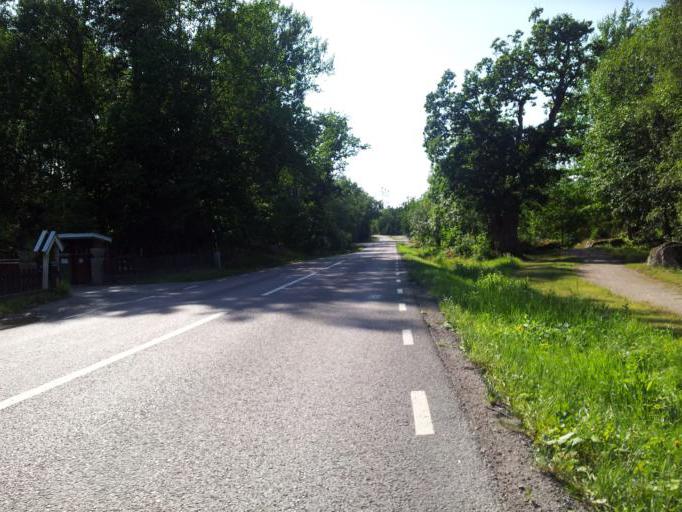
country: SE
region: Stockholm
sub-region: Norrtalje Kommun
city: Nykvarn
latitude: 59.8775
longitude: 18.0295
